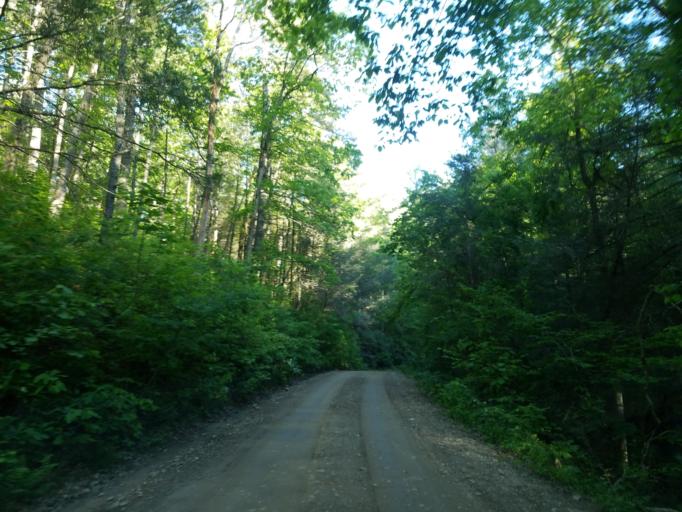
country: US
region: Georgia
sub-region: Lumpkin County
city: Dahlonega
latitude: 34.6930
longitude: -84.1411
